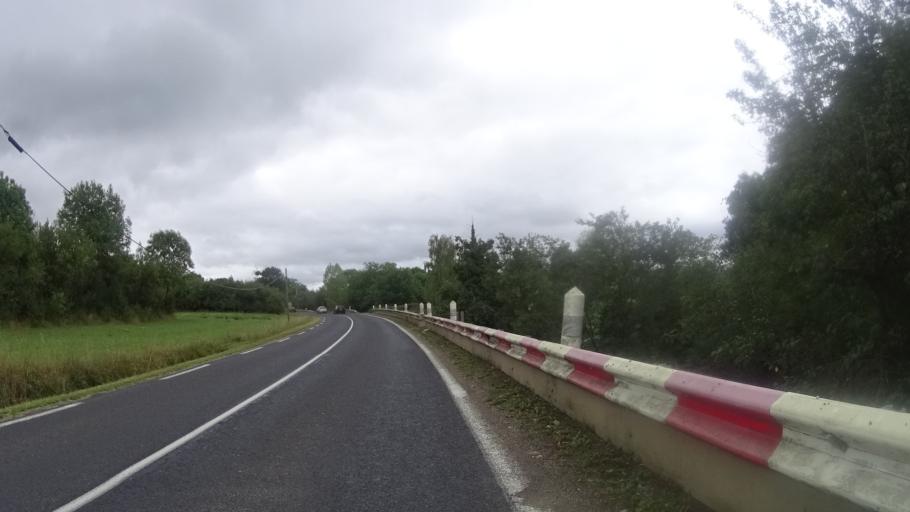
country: FR
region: Lorraine
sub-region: Departement de Meurthe-et-Moselle
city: Art-sur-Meurthe
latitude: 48.6511
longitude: 6.2708
